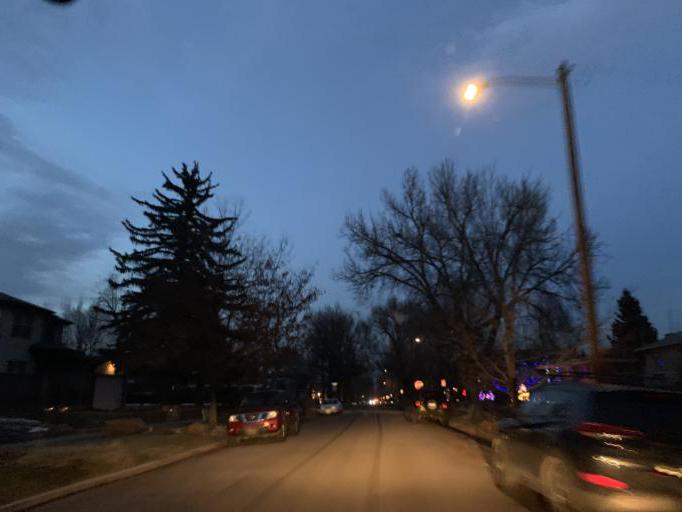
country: US
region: Colorado
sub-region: Jefferson County
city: Edgewater
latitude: 39.7719
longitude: -105.0416
